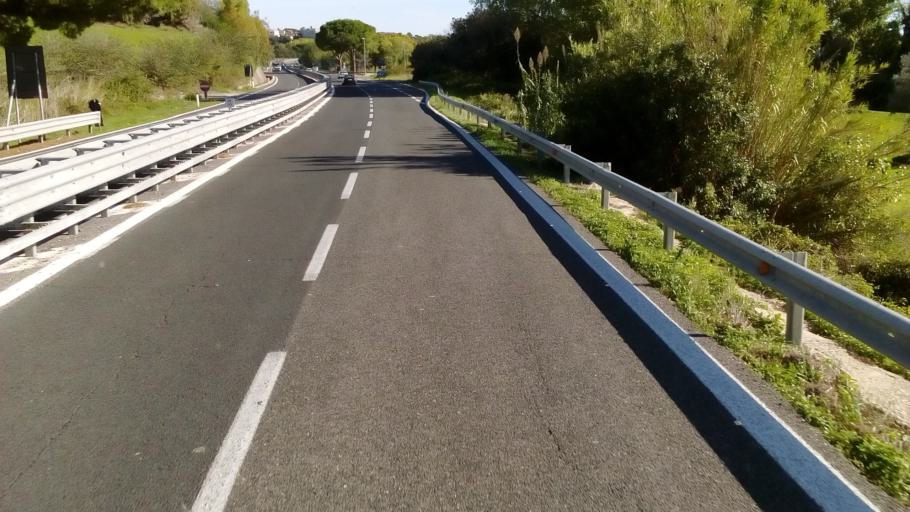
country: IT
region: Latium
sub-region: Provincia di Viterbo
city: Montalto di Castro
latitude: 42.3576
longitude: 11.5884
